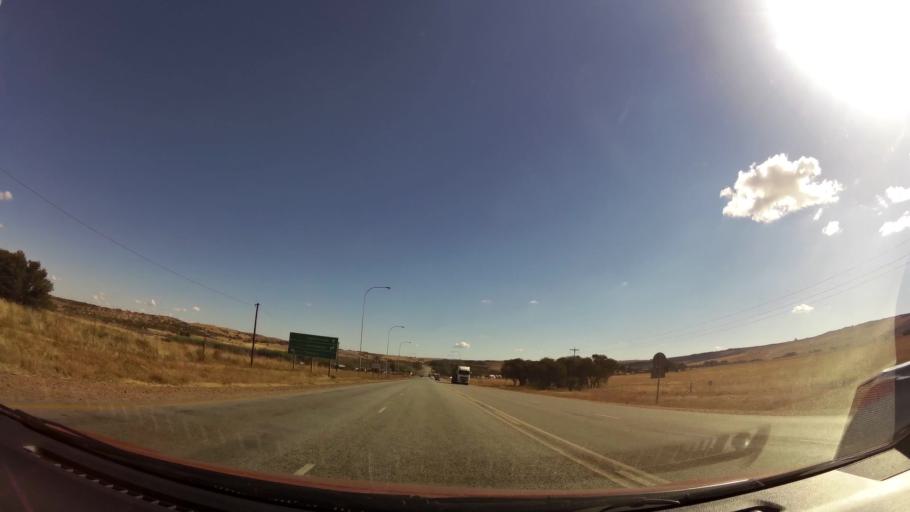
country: ZA
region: North-West
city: Fochville
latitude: -26.4413
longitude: 27.4873
